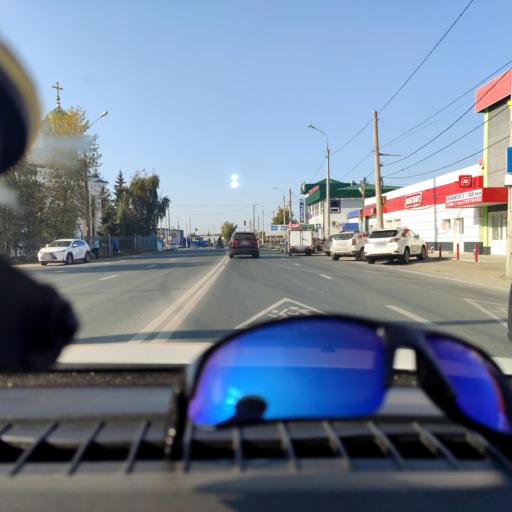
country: RU
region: Samara
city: Volzhskiy
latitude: 53.4254
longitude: 50.1230
